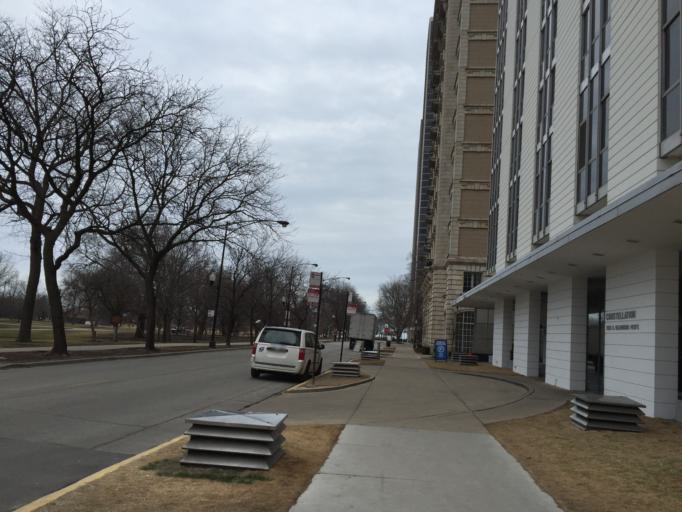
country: US
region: Illinois
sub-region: Cook County
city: Chicago
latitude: 41.9112
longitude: -87.6301
